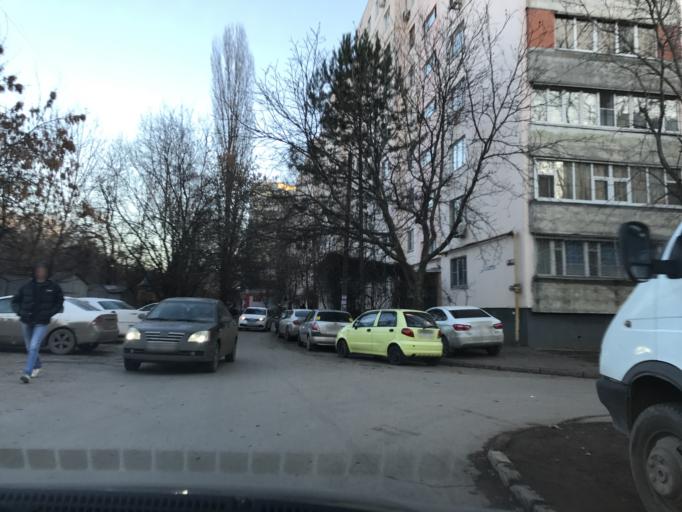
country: RU
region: Rostov
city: Rostov-na-Donu
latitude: 47.2318
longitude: 39.6219
